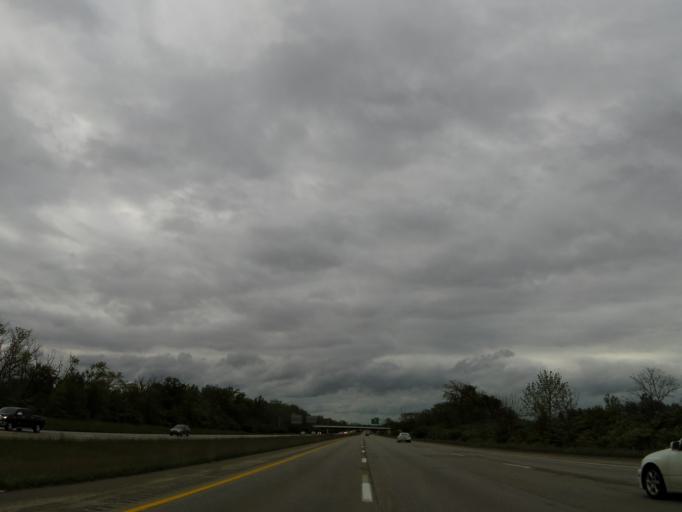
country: US
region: Ohio
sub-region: Franklin County
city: Grove City
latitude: 39.8983
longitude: -83.0324
